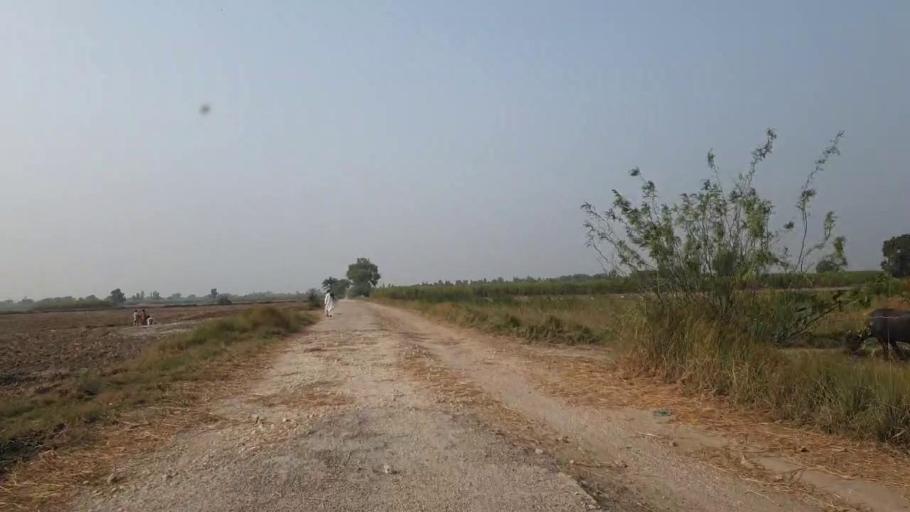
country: PK
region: Sindh
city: Matli
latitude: 25.0753
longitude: 68.5922
